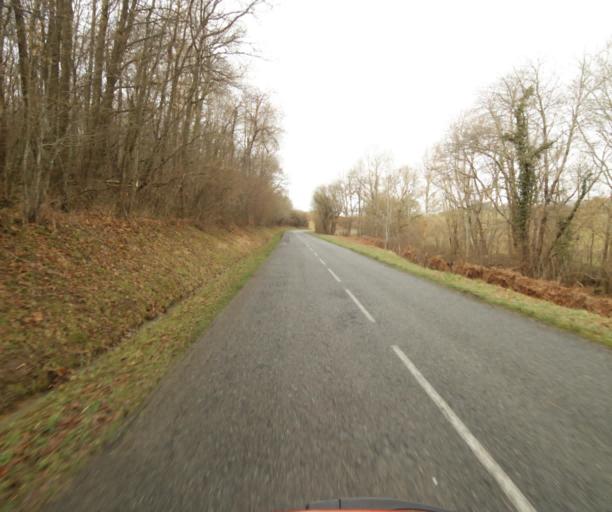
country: FR
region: Midi-Pyrenees
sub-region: Departement de l'Ariege
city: Pamiers
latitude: 43.1467
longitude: 1.5247
